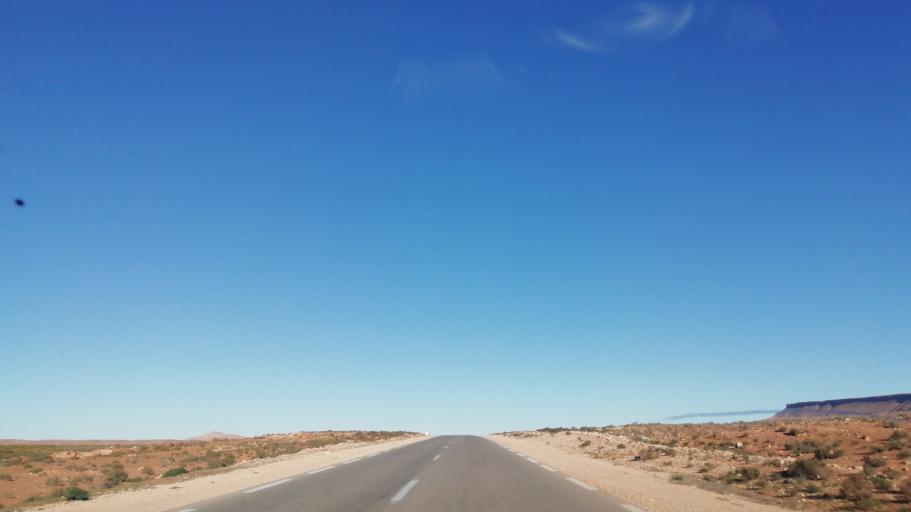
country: DZ
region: El Bayadh
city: El Abiodh Sidi Cheikh
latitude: 33.0905
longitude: 0.1910
